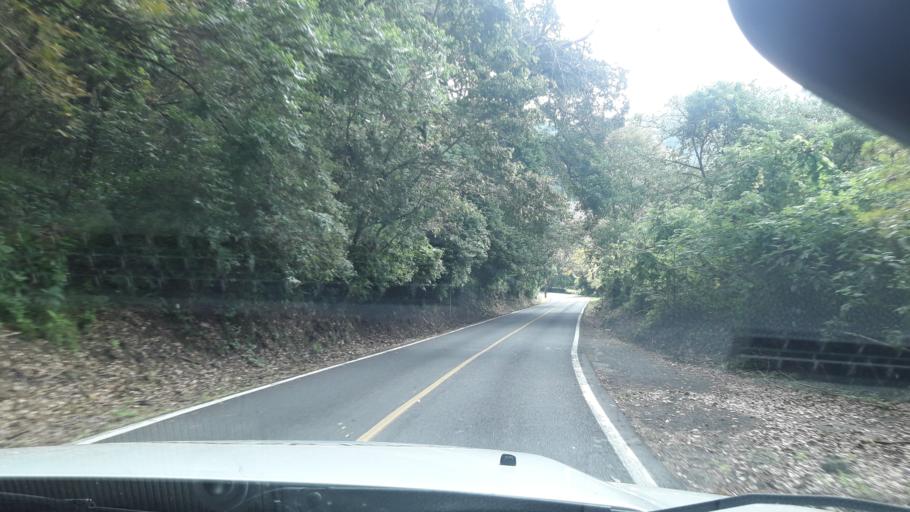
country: MX
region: Colima
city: Suchitlan
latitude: 19.4482
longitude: -103.7178
